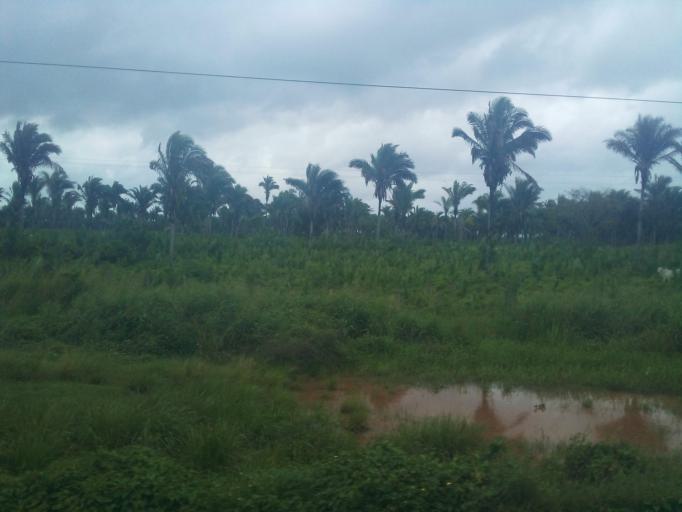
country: BR
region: Maranhao
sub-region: Arari
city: Arari
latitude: -3.5750
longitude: -44.7063
